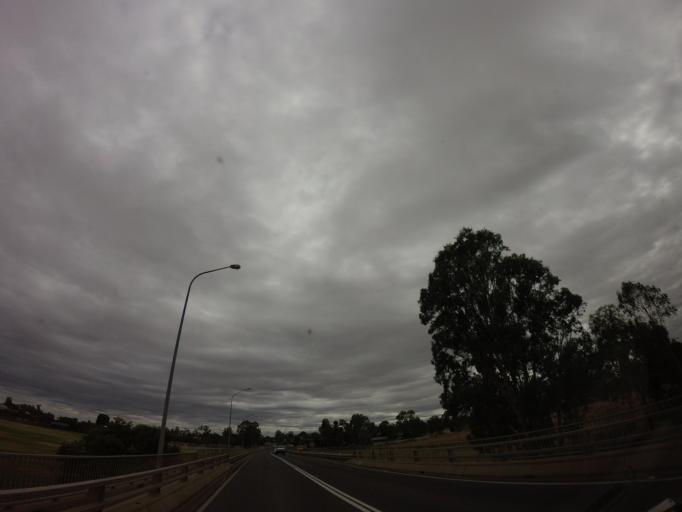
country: AU
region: New South Wales
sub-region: Narrabri
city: Narrabri
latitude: -30.3431
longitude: 149.7631
